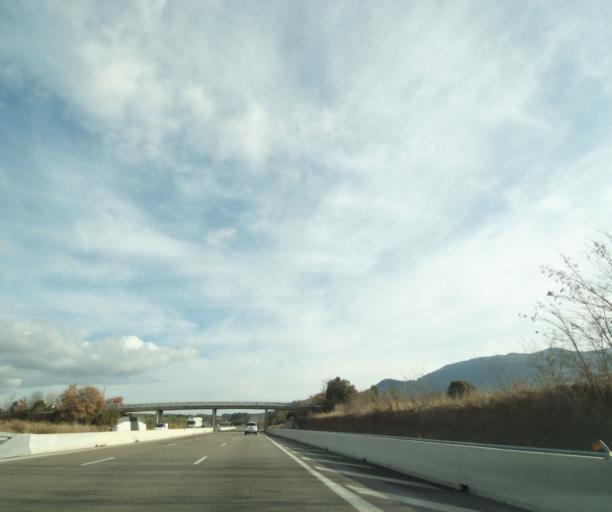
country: FR
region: Provence-Alpes-Cote d'Azur
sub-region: Departement du Var
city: Pourrieres
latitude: 43.4807
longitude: 5.7428
